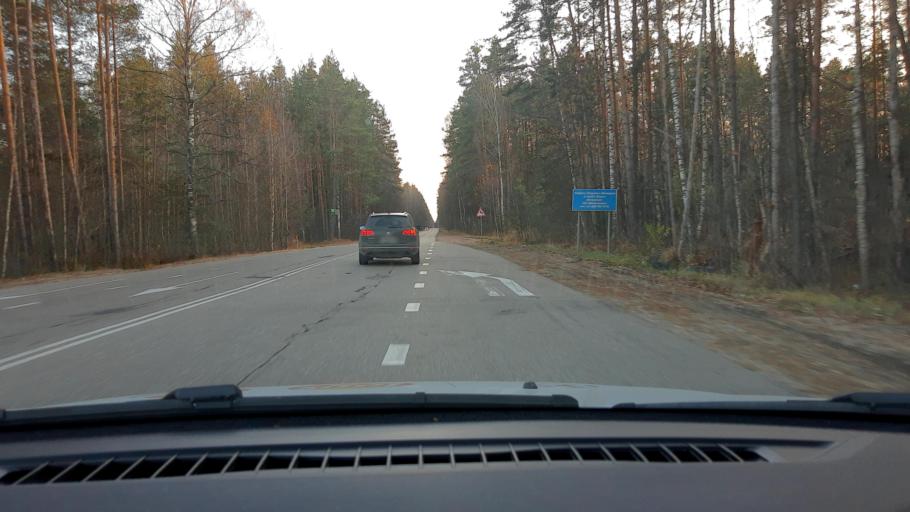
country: RU
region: Nizjnij Novgorod
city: Volodarsk
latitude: 56.2835
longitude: 43.1657
